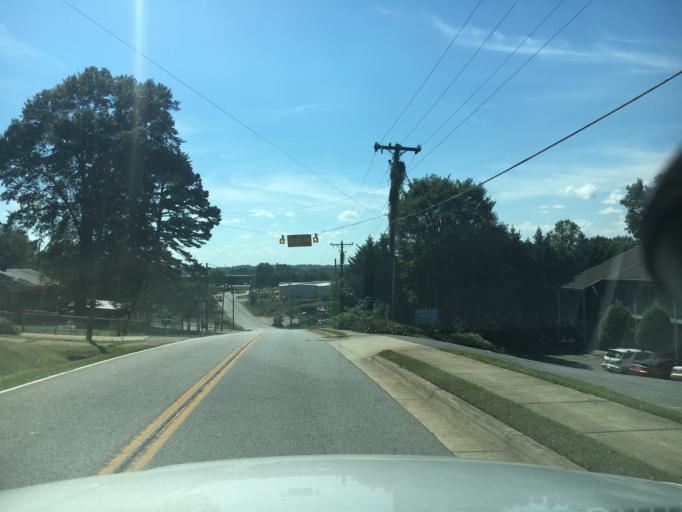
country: US
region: North Carolina
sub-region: Catawba County
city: Hickory
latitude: 35.7250
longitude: -81.3540
